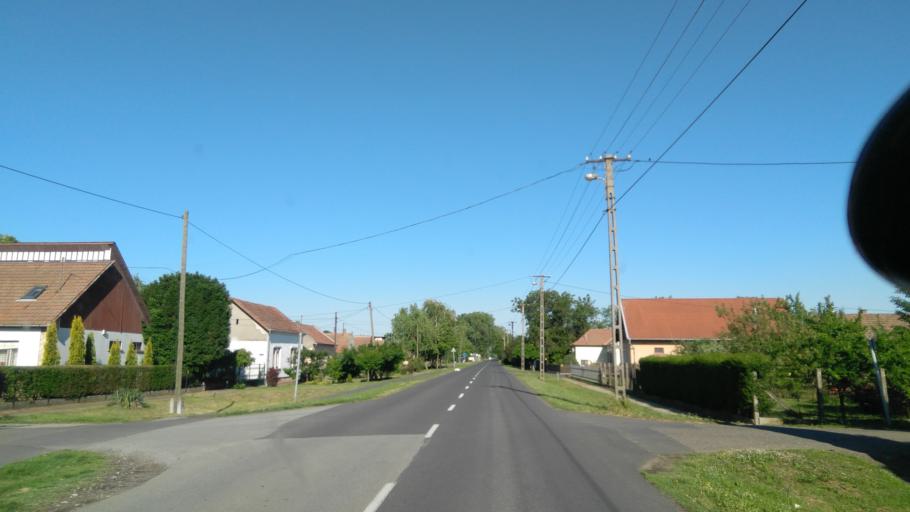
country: HU
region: Bekes
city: Elek
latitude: 46.5329
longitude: 21.2363
